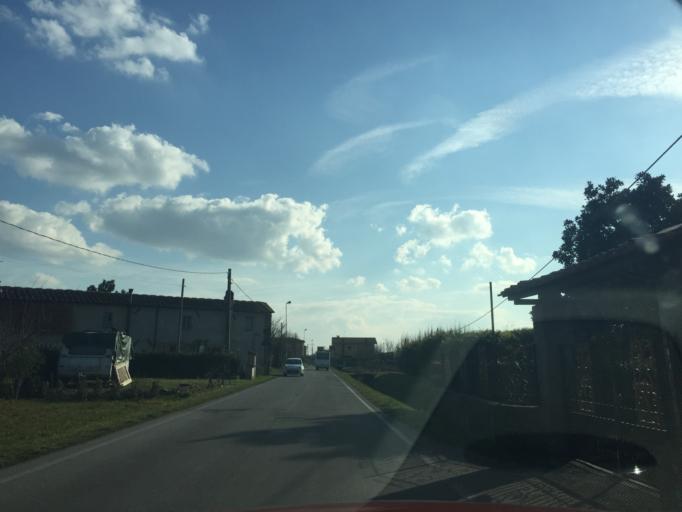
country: IT
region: Tuscany
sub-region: Provincia di Pistoia
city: Ponte Buggianese
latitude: 43.8336
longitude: 10.7430
